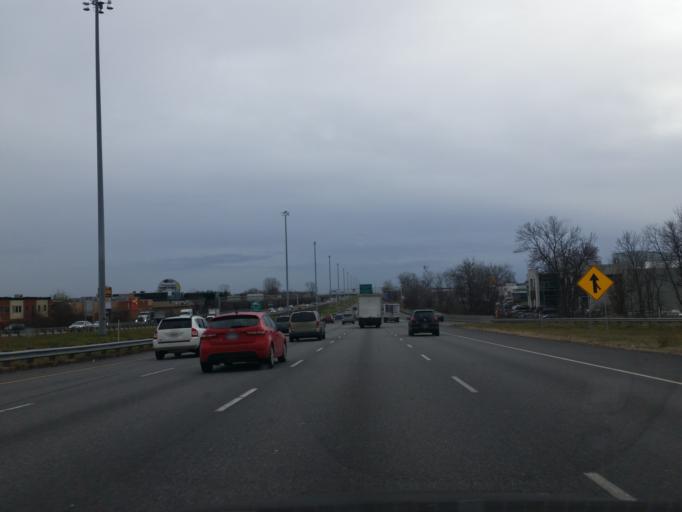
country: CA
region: Quebec
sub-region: Laurentides
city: Blainville
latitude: 45.6445
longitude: -73.8658
